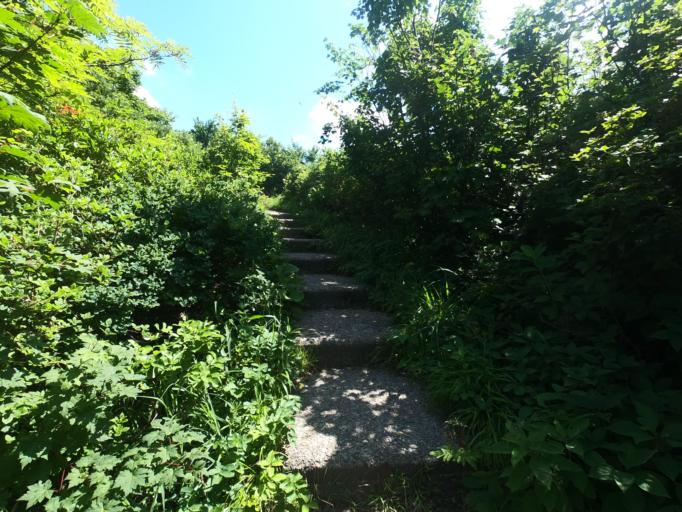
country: JP
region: Akita
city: Yuzawa
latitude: 38.9790
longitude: 140.7714
